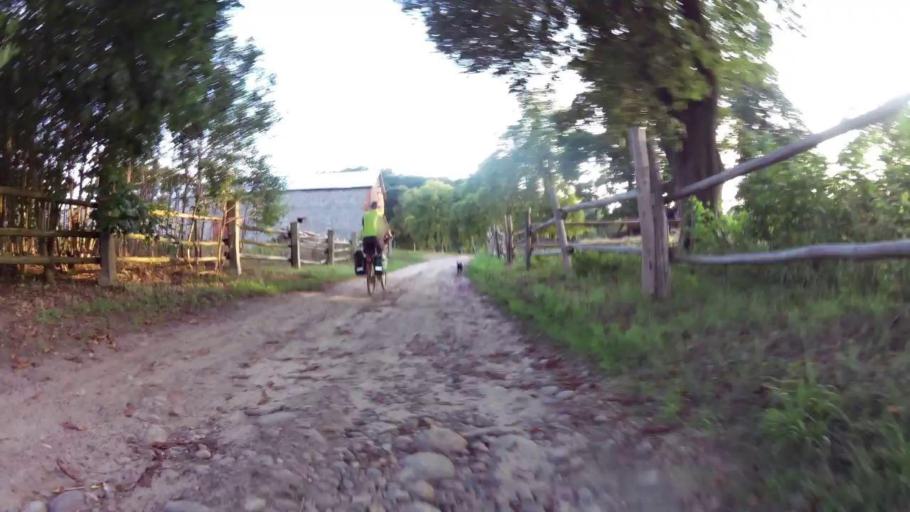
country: PL
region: West Pomeranian Voivodeship
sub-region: Powiat drawski
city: Drawsko Pomorskie
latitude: 53.4977
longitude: 15.7478
